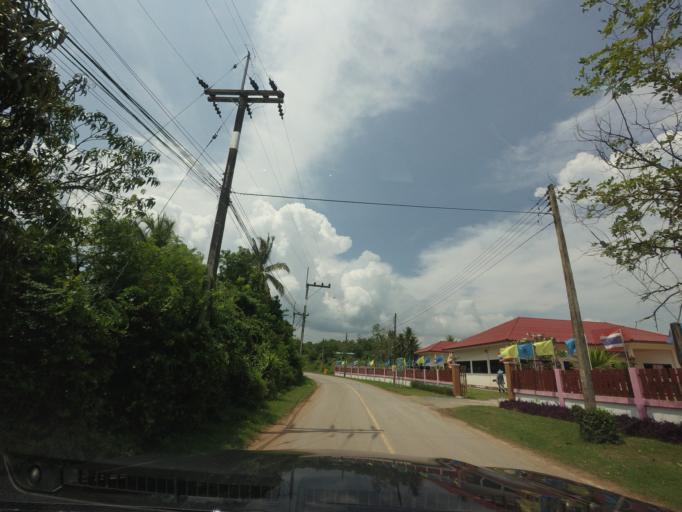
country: TH
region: Khon Kaen
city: Wiang Kao
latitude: 16.6799
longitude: 102.2871
